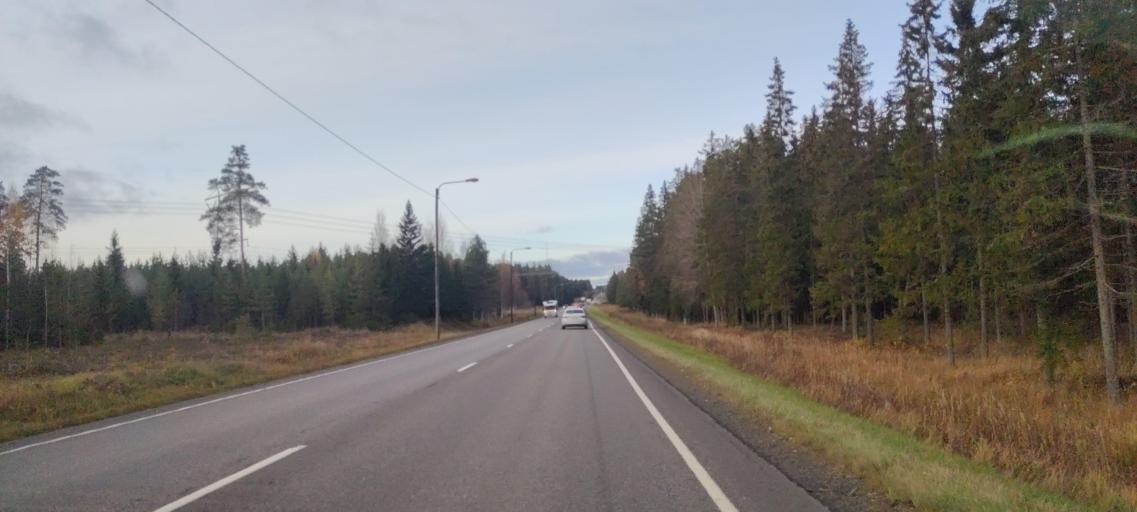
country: FI
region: Satakunta
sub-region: Rauma
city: Eurajoki
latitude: 61.2413
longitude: 21.7137
